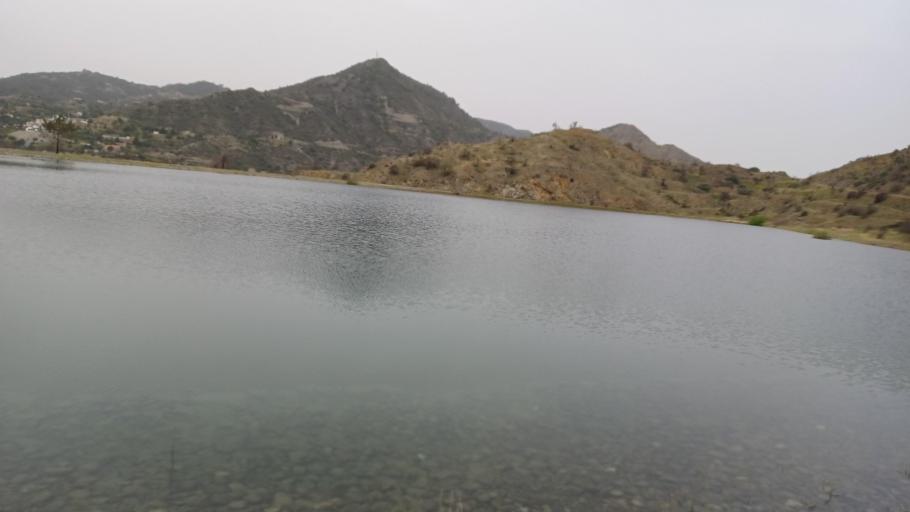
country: CY
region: Limassol
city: Parekklisha
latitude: 34.8394
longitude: 33.1223
